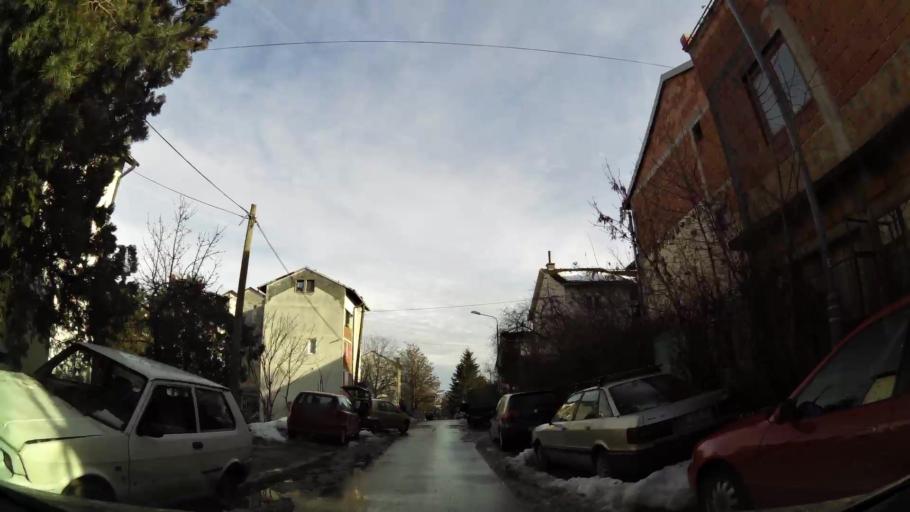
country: RS
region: Central Serbia
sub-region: Belgrade
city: Rakovica
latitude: 44.7218
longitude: 20.4247
